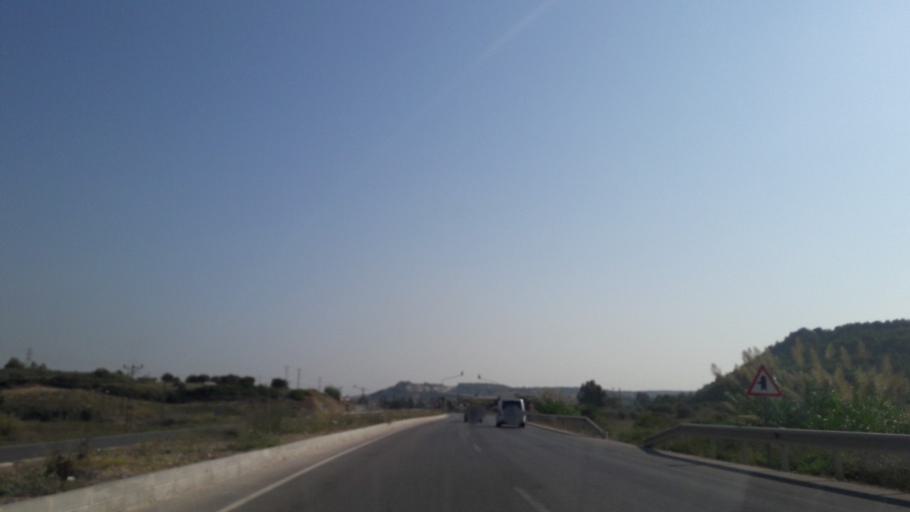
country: TR
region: Adana
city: Yuregir
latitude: 37.0693
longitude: 35.4549
